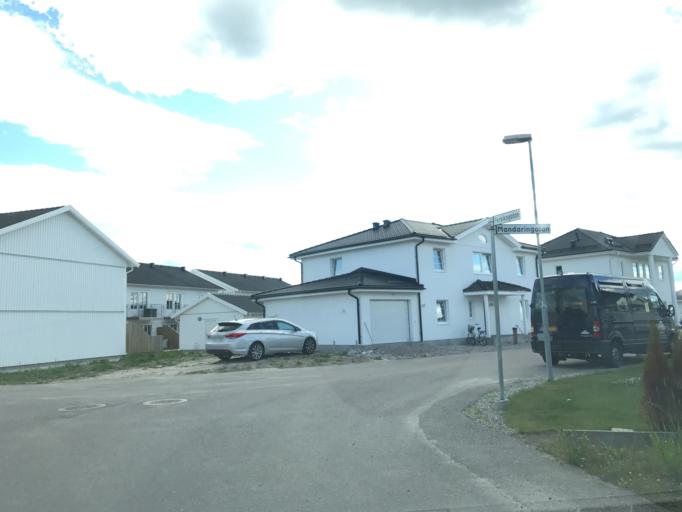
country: SE
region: OErebro
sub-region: Orebro Kommun
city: Orebro
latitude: 59.3029
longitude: 15.1607
